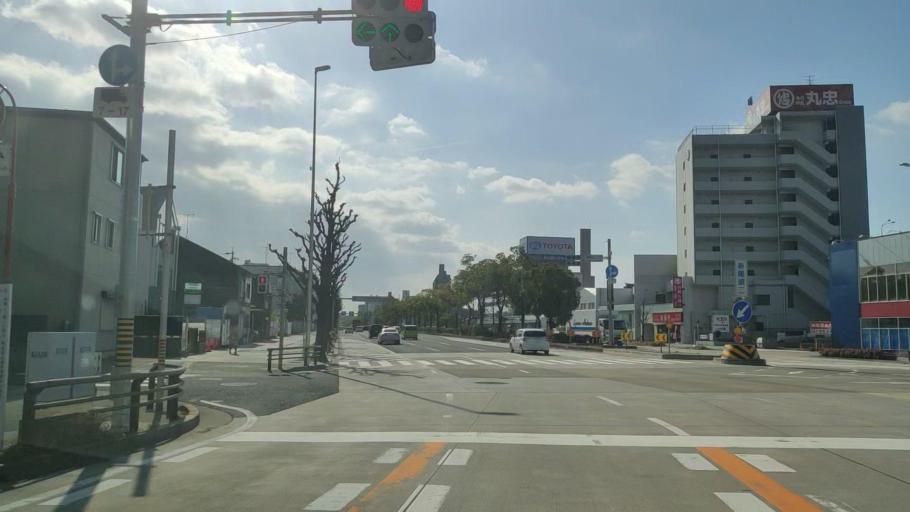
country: JP
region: Aichi
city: Nagoya-shi
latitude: 35.1373
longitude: 136.9001
